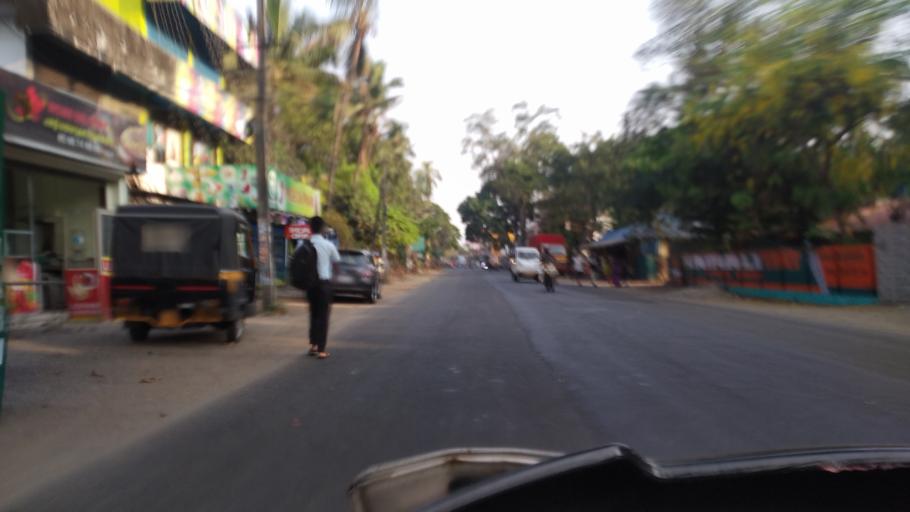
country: IN
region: Kerala
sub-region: Thrissur District
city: Thanniyam
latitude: 10.4061
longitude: 76.1108
